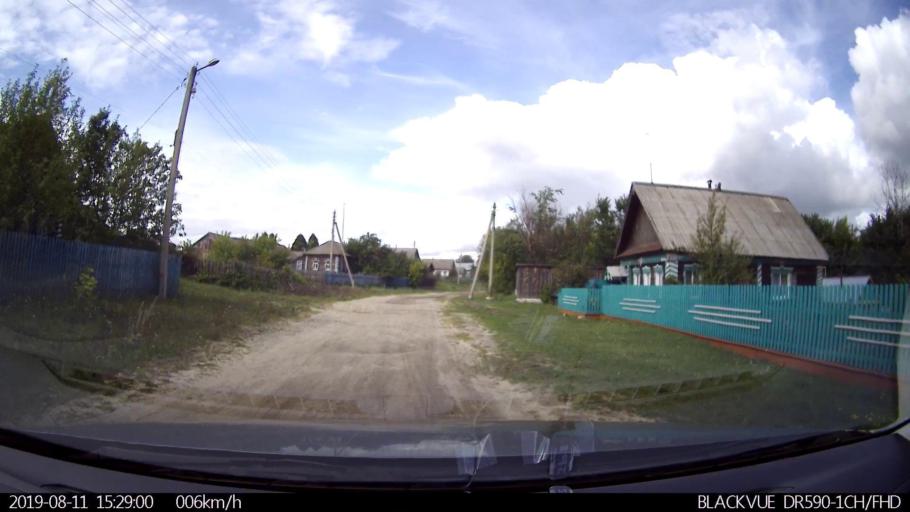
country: RU
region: Ulyanovsk
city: Ignatovka
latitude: 53.8533
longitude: 47.5743
